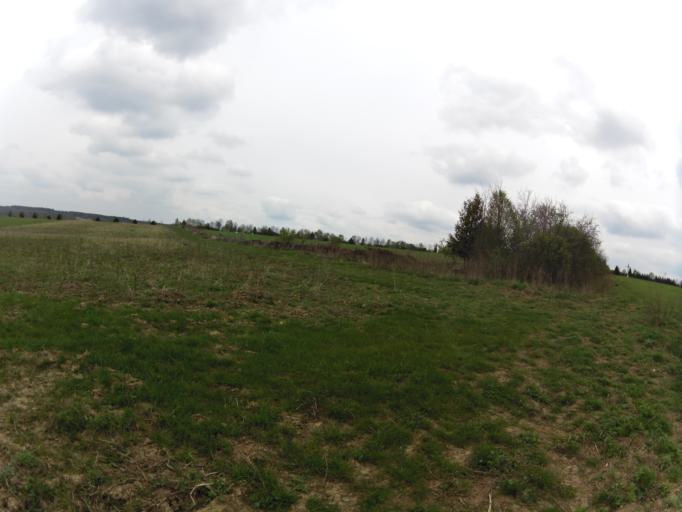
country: DE
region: Bavaria
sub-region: Regierungsbezirk Unterfranken
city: Greussenheim
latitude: 49.8290
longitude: 9.7962
